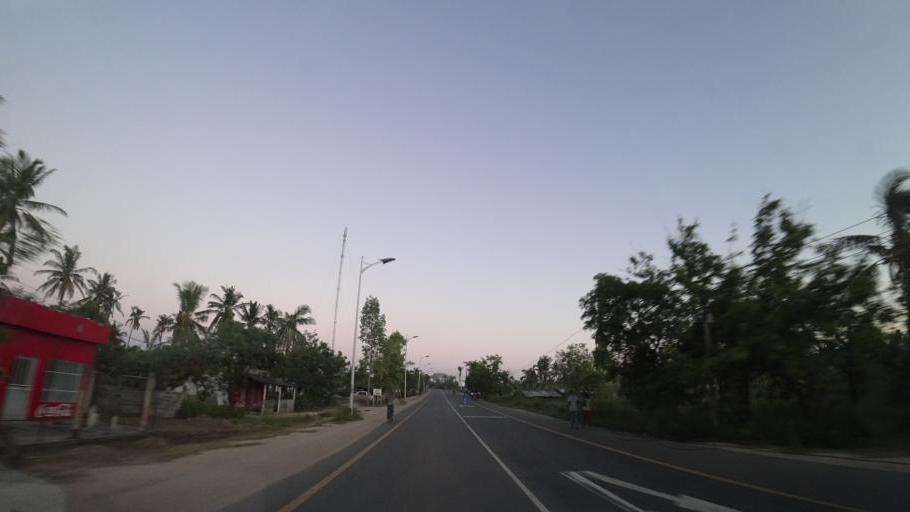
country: MZ
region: Sofala
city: Dondo
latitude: -19.5308
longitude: 34.6285
